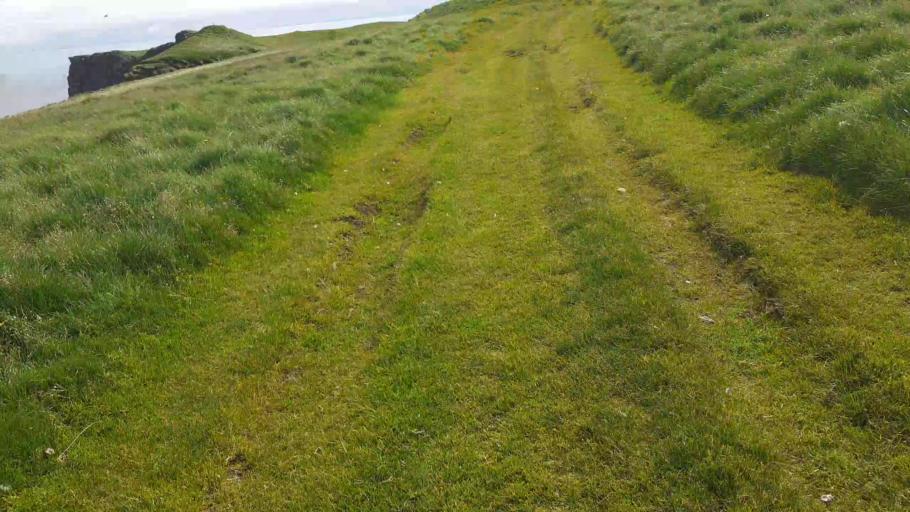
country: IS
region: Northeast
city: Dalvik
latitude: 66.5498
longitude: -17.9924
